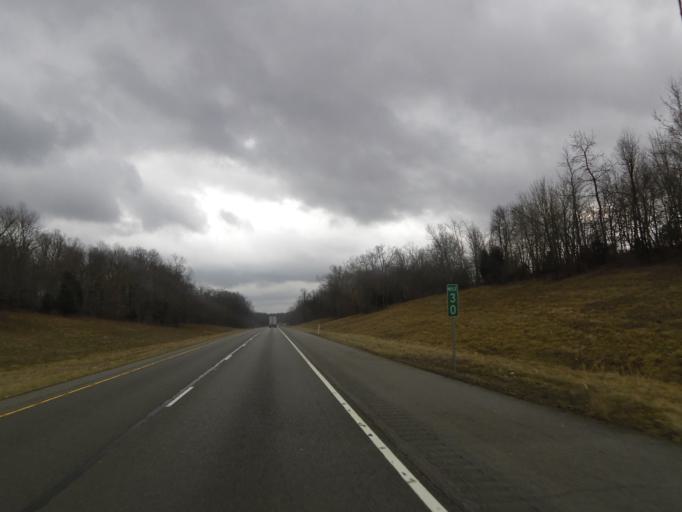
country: US
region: Illinois
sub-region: Massac County
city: Metropolis
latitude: 37.2598
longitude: -88.7300
